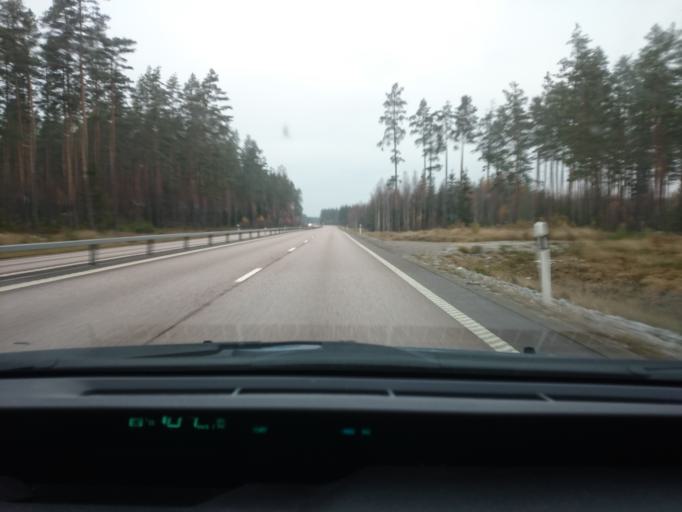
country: SE
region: Dalarna
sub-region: Avesta Kommun
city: Avesta
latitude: 60.0526
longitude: 16.3387
